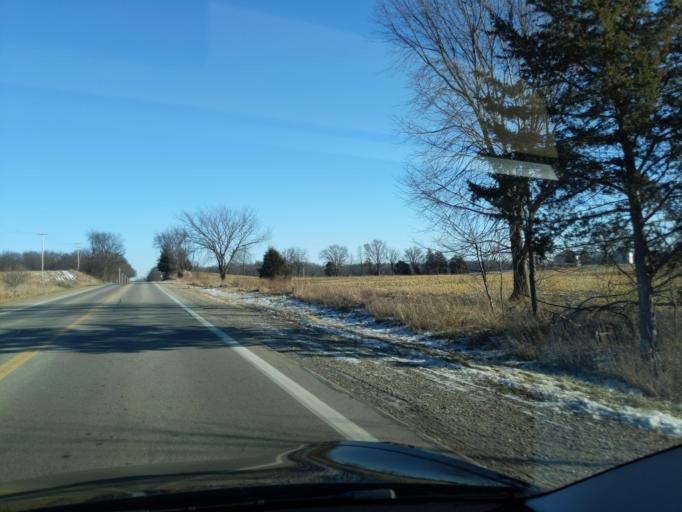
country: US
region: Michigan
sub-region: Ingham County
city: Stockbridge
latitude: 42.3942
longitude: -84.2999
